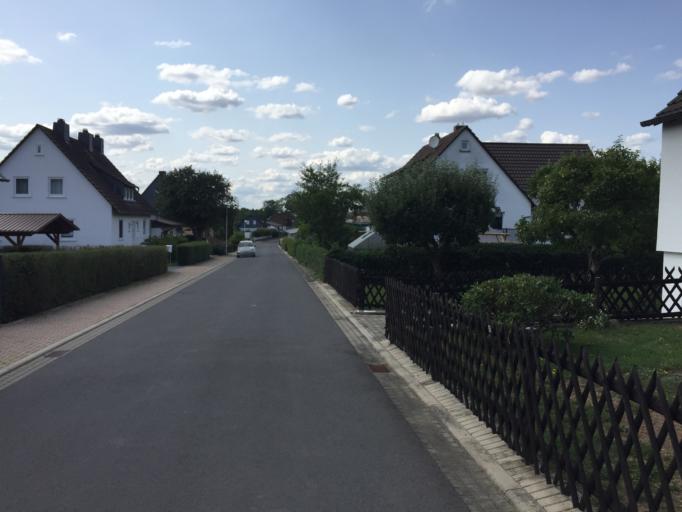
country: DE
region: Hesse
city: Schwalmstadt
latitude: 50.9017
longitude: 9.2710
